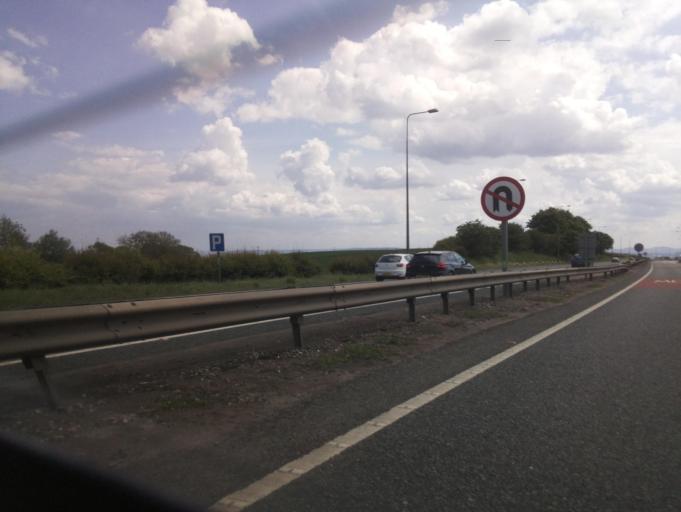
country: GB
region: England
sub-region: Hartlepool
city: Elwick
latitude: 54.6776
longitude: -1.3008
